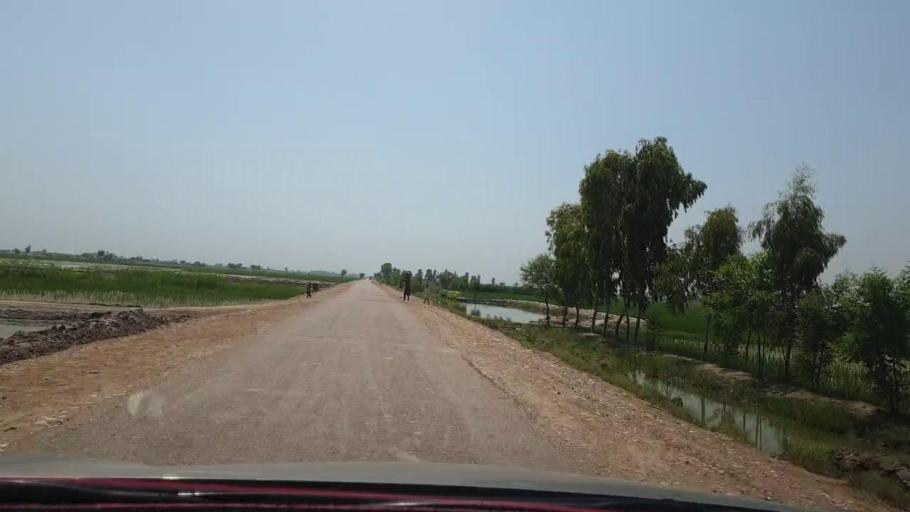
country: PK
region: Sindh
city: Warah
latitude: 27.5643
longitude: 67.8017
